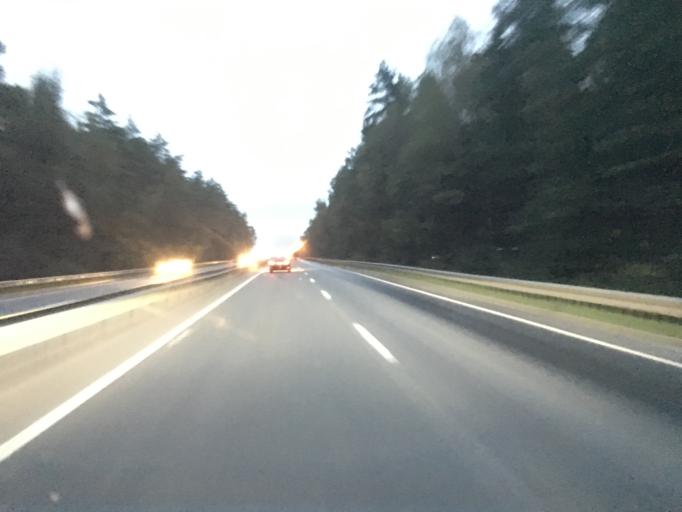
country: RU
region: Kaluga
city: Maloyaroslavets
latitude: 54.9718
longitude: 36.4811
